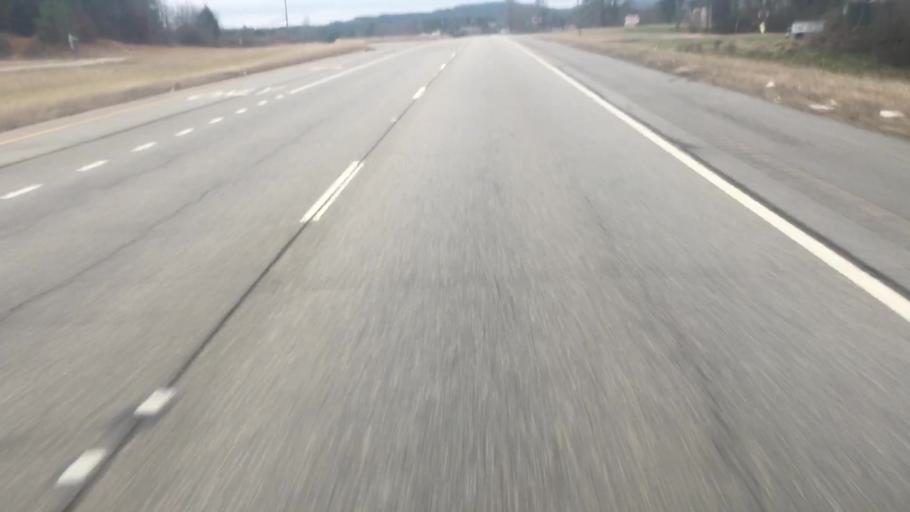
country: US
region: Alabama
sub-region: Walker County
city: Dora
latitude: 33.7975
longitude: -87.1119
